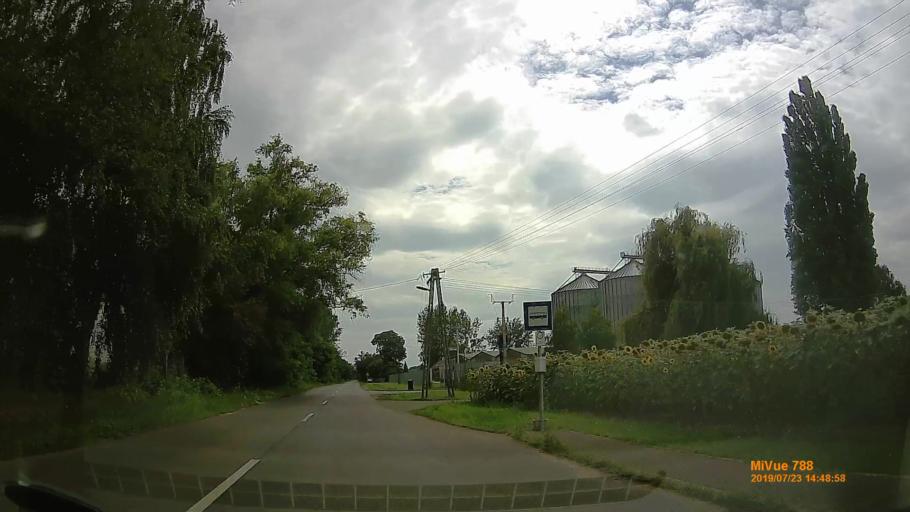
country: HU
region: Szabolcs-Szatmar-Bereg
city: Nyiregyhaza
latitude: 47.8992
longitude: 21.6650
